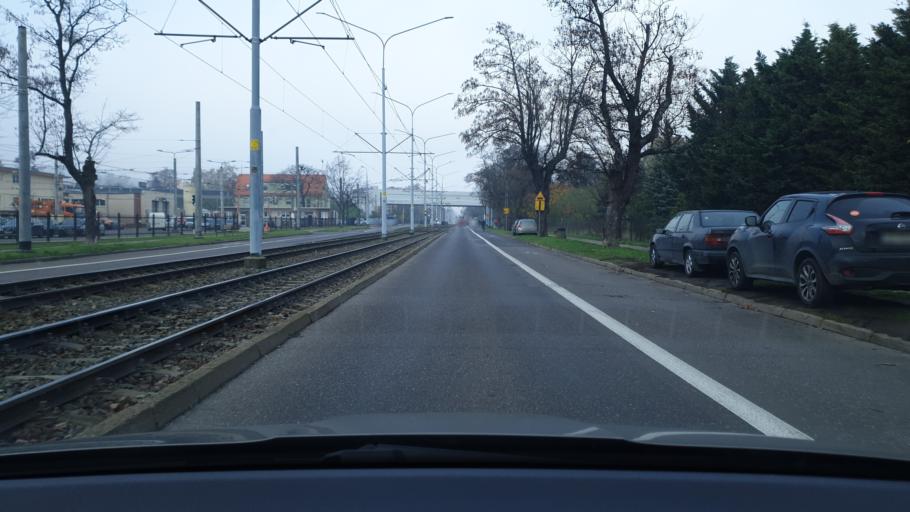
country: PL
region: Pomeranian Voivodeship
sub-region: Sopot
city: Sopot
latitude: 54.3897
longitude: 18.5798
